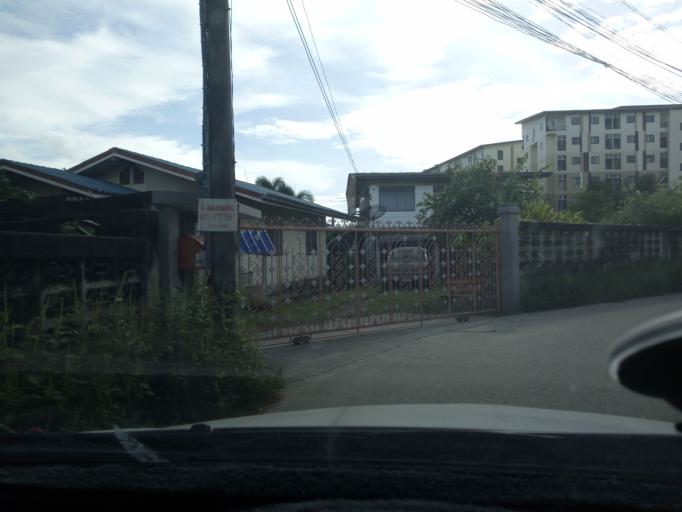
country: TH
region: Chon Buri
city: Phan Thong
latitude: 13.4166
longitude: 101.0665
